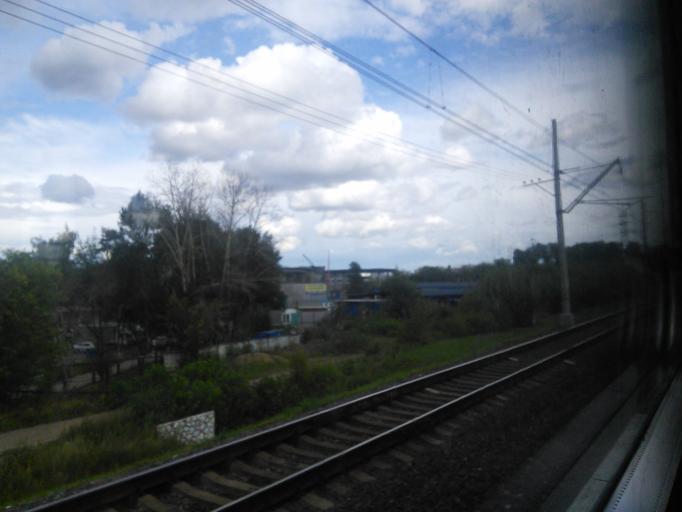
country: RU
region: Moscow
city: Ryazanskiy
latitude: 55.7469
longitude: 37.7328
